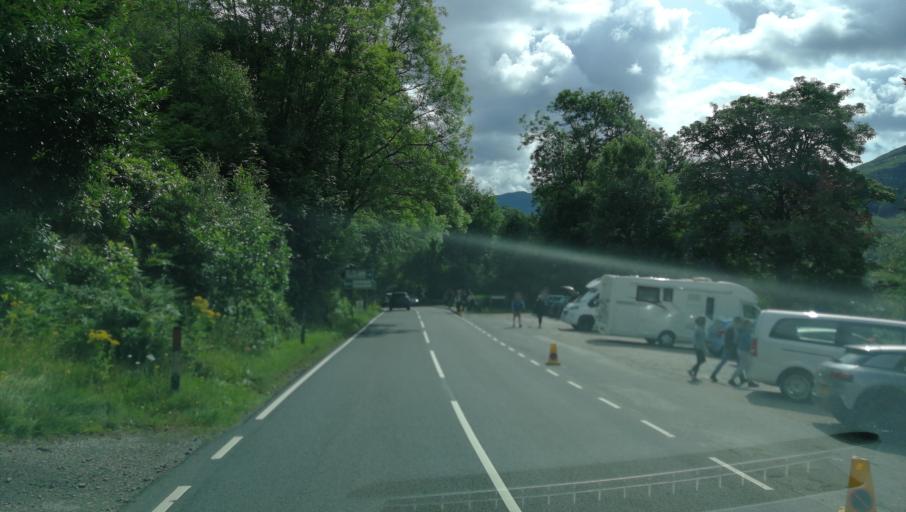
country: GB
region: Scotland
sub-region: Highland
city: Fort William
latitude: 56.8719
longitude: -5.4415
